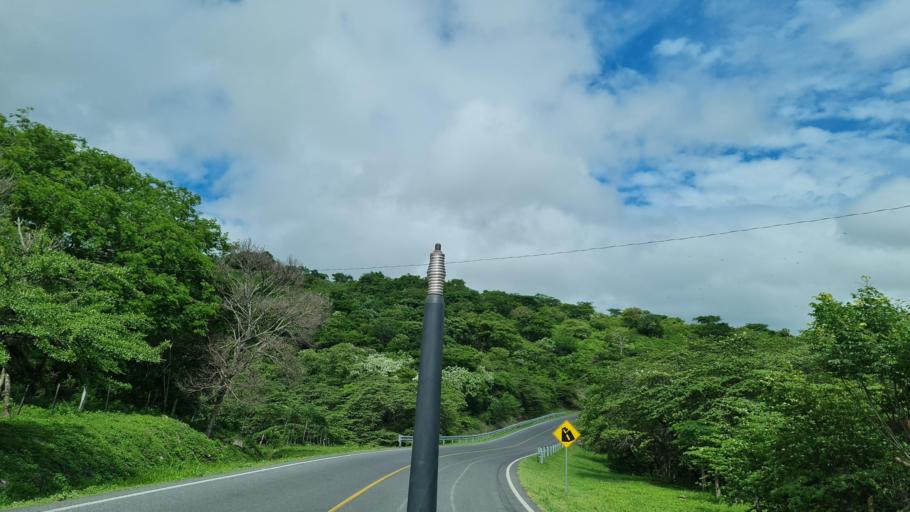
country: NI
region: Boaco
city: San Jose de los Remates
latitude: 12.6110
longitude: -85.8878
